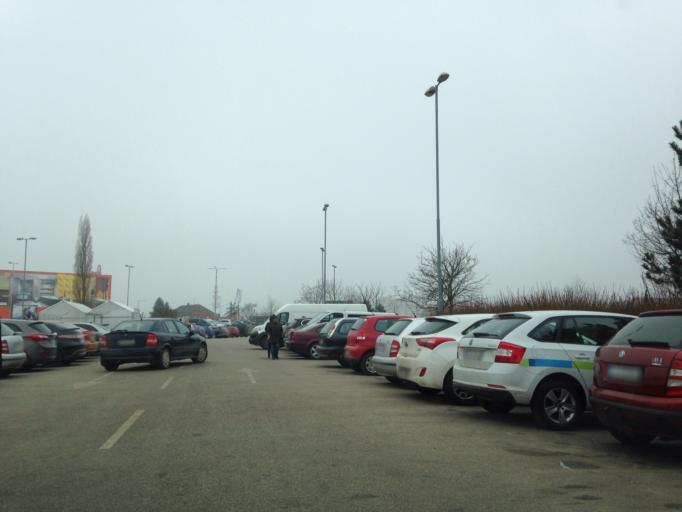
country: SK
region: Nitriansky
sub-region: Okres Nove Zamky
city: Nove Zamky
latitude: 47.9853
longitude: 18.1777
